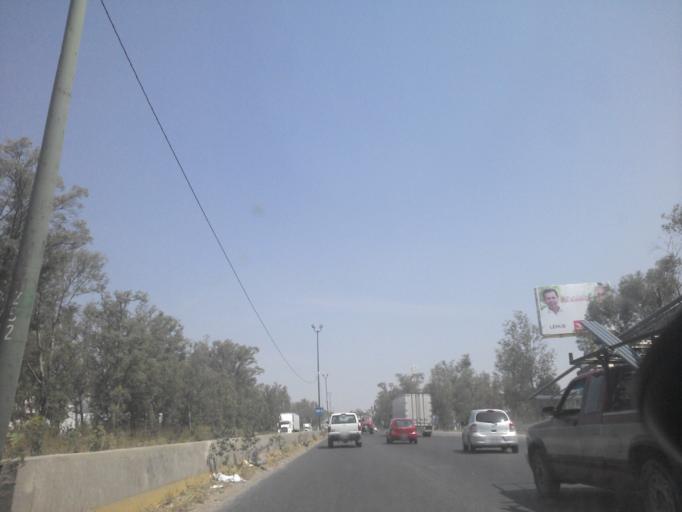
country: MX
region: Jalisco
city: Guadalajara
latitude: 20.6439
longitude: -103.4415
